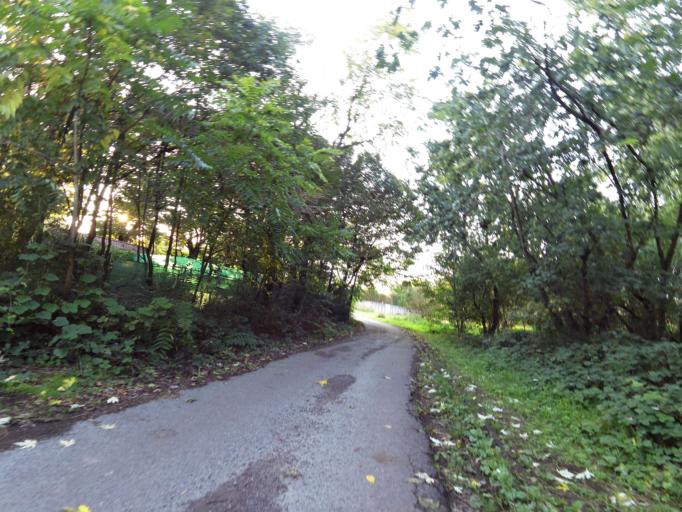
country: IT
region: Lombardy
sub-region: Citta metropolitana di Milano
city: Bettola-Zeloforomagno
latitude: 45.4185
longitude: 9.2896
